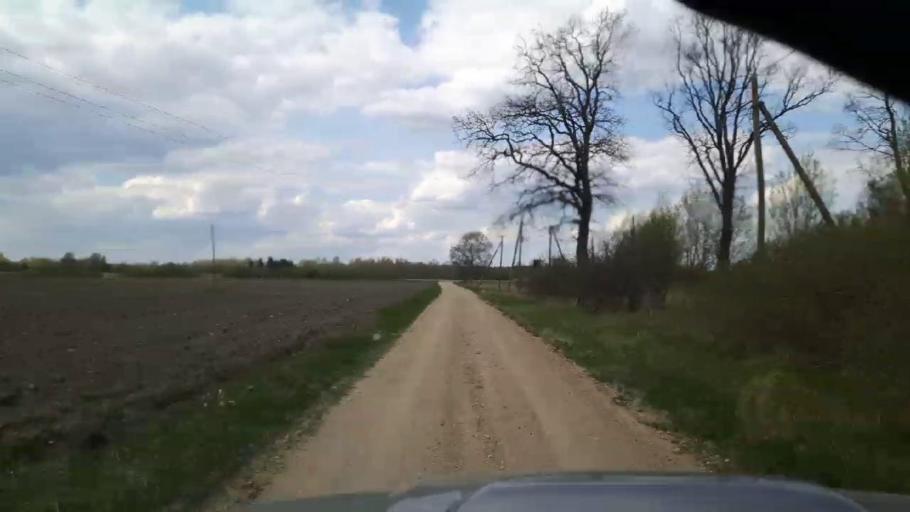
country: EE
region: Paernumaa
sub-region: Sindi linn
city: Sindi
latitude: 58.4161
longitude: 24.7001
